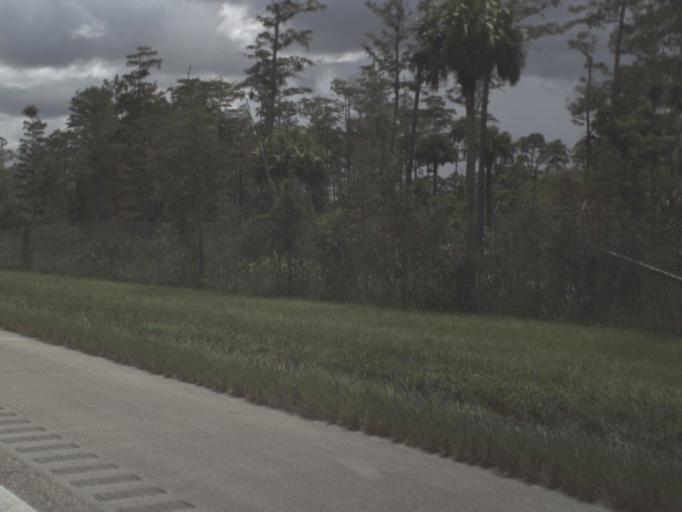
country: US
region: Florida
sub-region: Collier County
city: Immokalee
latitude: 26.1550
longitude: -81.2977
